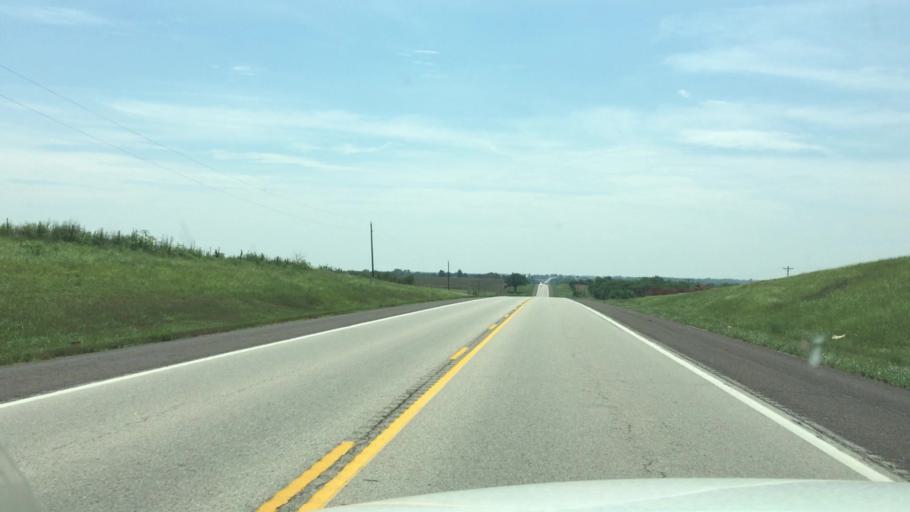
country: US
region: Kansas
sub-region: Jackson County
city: Holton
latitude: 39.6080
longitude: -95.7318
